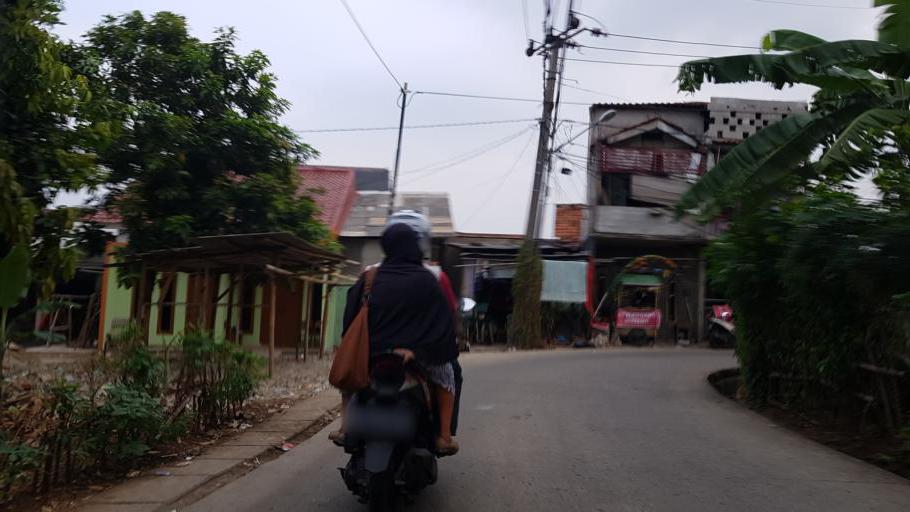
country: ID
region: West Java
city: Sawangan
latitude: -6.3793
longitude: 106.7947
